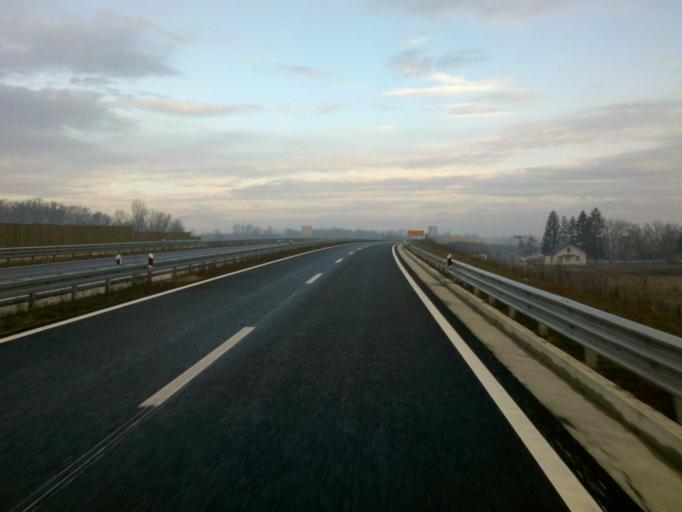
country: HR
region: Zagrebacka
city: Dubrava
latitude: 45.9106
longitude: 16.5035
